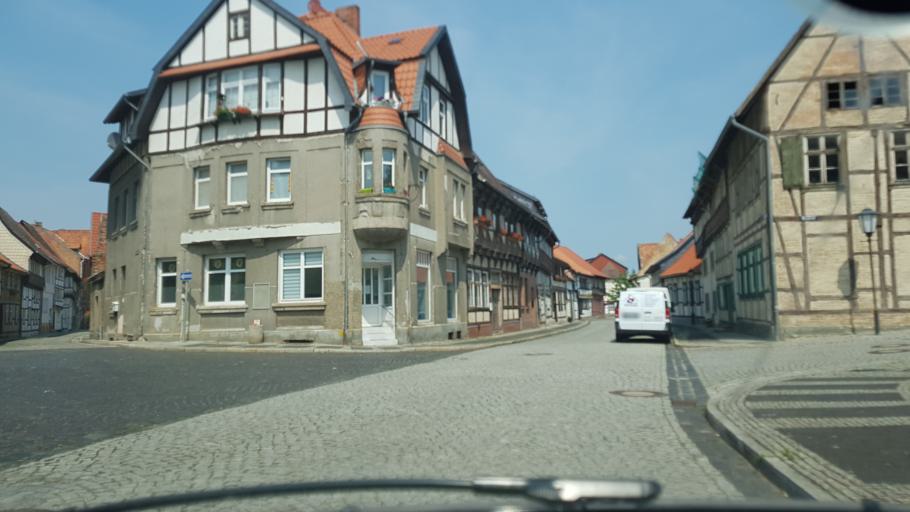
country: DE
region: Saxony-Anhalt
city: Osterwieck
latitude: 51.9671
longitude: 10.7119
